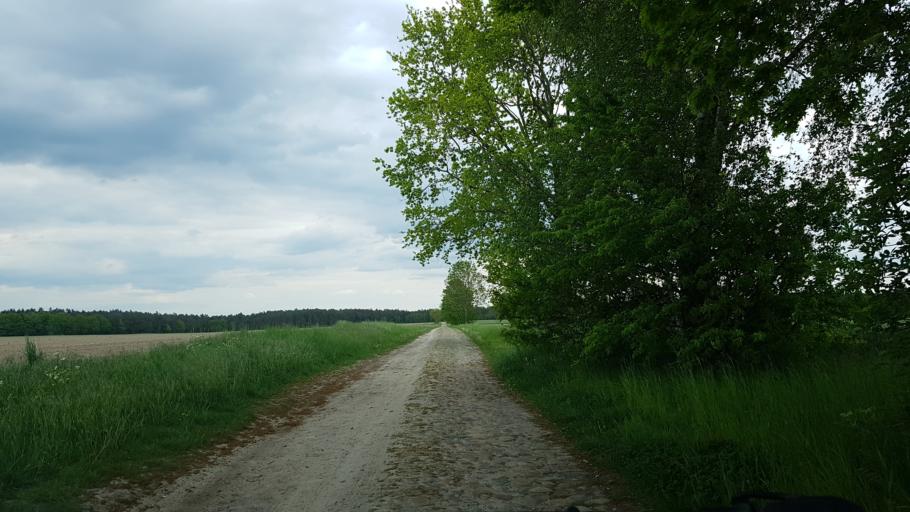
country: DE
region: Lower Saxony
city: Vastorf
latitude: 53.1855
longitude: 10.5563
